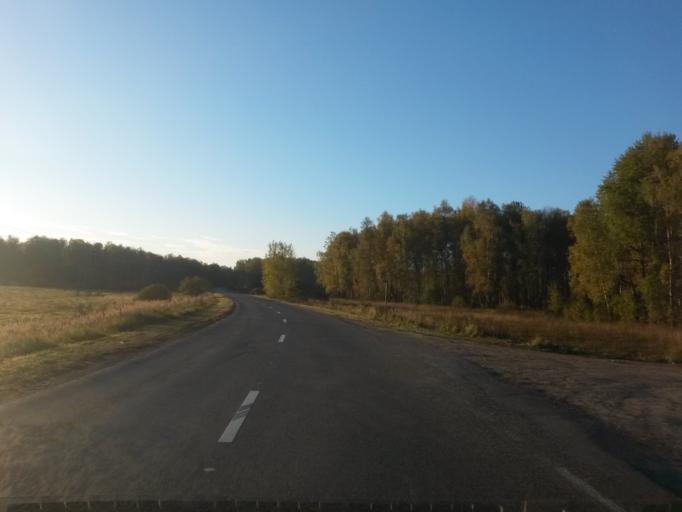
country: RU
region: Moskovskaya
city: Lyubuchany
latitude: 55.2343
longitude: 37.6443
